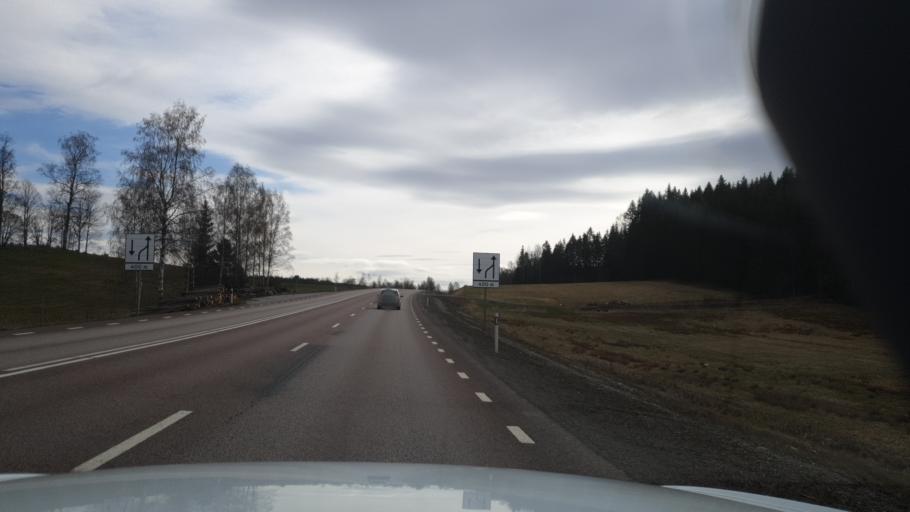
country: SE
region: Vaermland
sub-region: Arvika Kommun
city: Arvika
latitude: 59.6691
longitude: 12.8095
